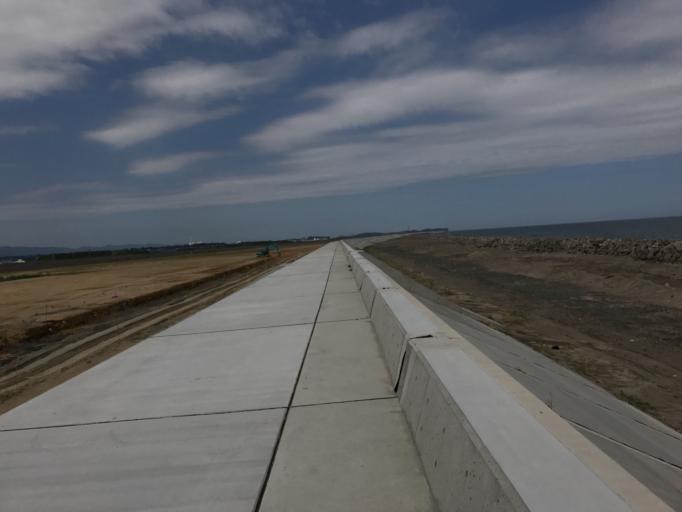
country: JP
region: Miyagi
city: Marumori
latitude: 37.7747
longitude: 140.9882
